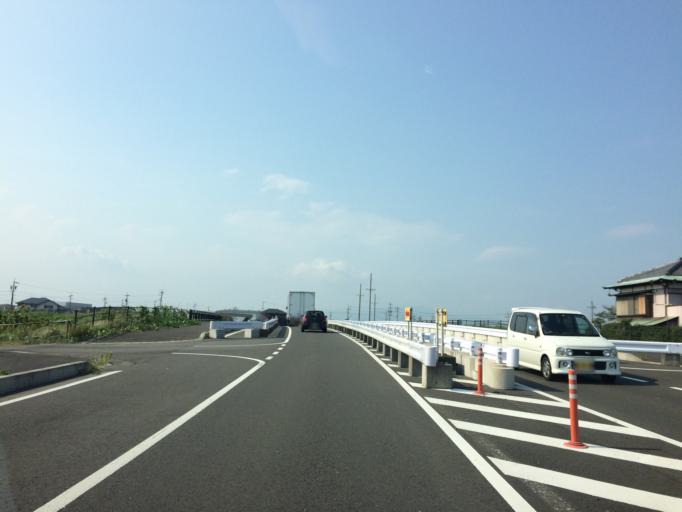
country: JP
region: Shizuoka
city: Yaizu
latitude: 34.8148
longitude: 138.3111
